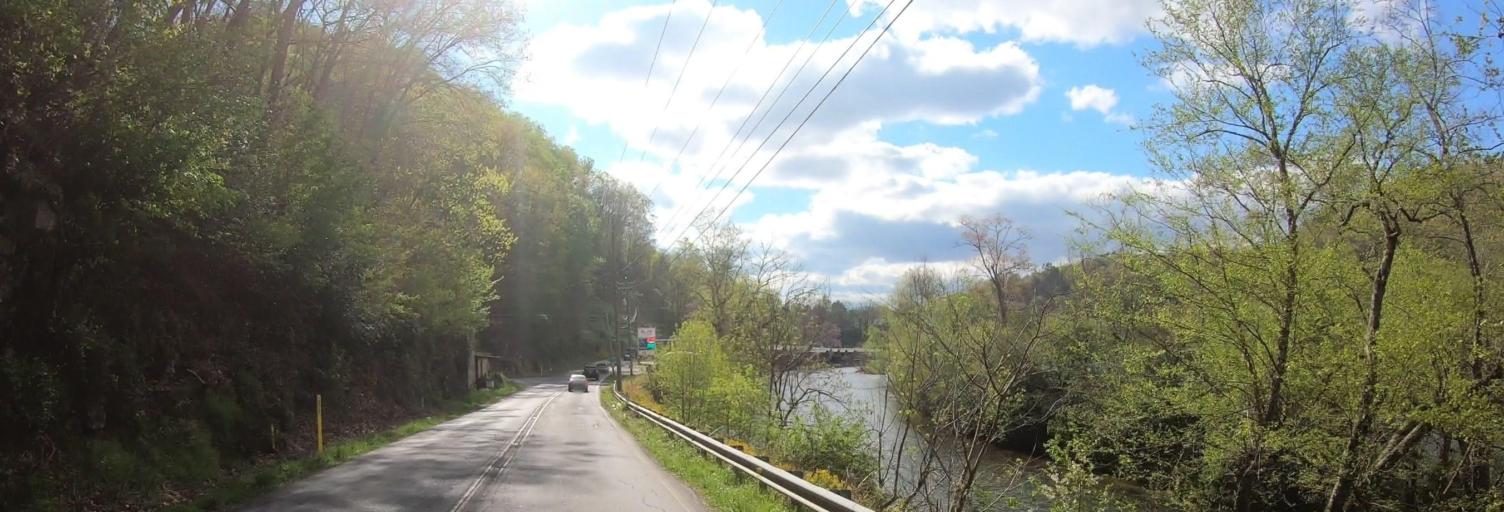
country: US
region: North Carolina
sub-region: Swain County
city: Bryson City
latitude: 35.4304
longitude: -83.4210
